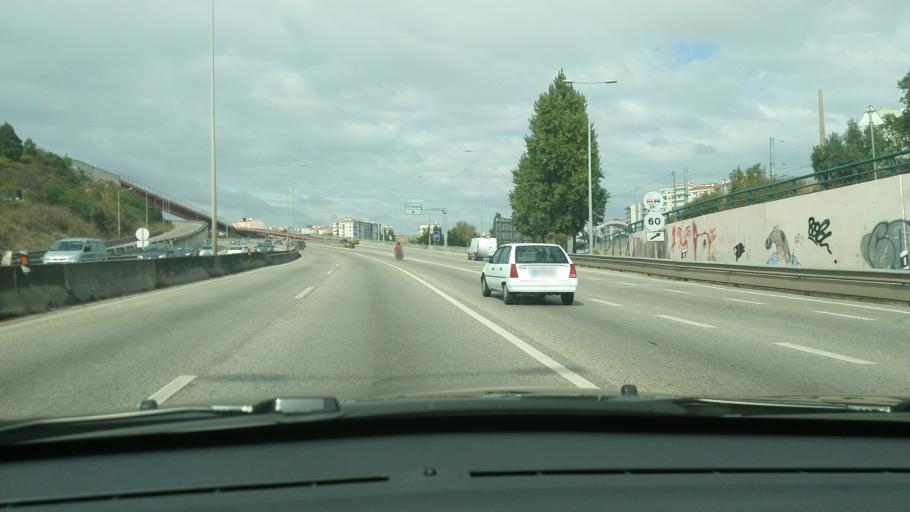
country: PT
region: Lisbon
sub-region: Sintra
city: Cacem
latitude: 38.7636
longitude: -9.2975
